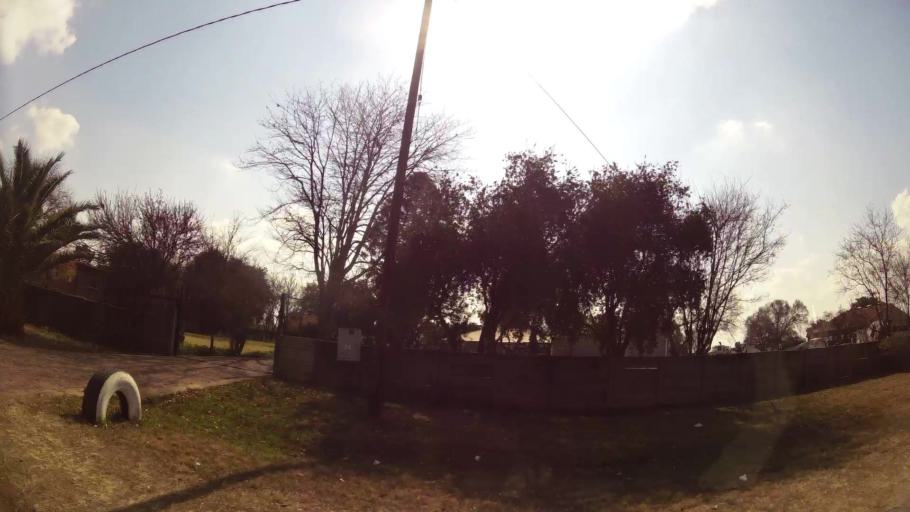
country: ZA
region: Mpumalanga
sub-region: Nkangala District Municipality
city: Delmas
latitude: -26.1872
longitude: 28.5383
